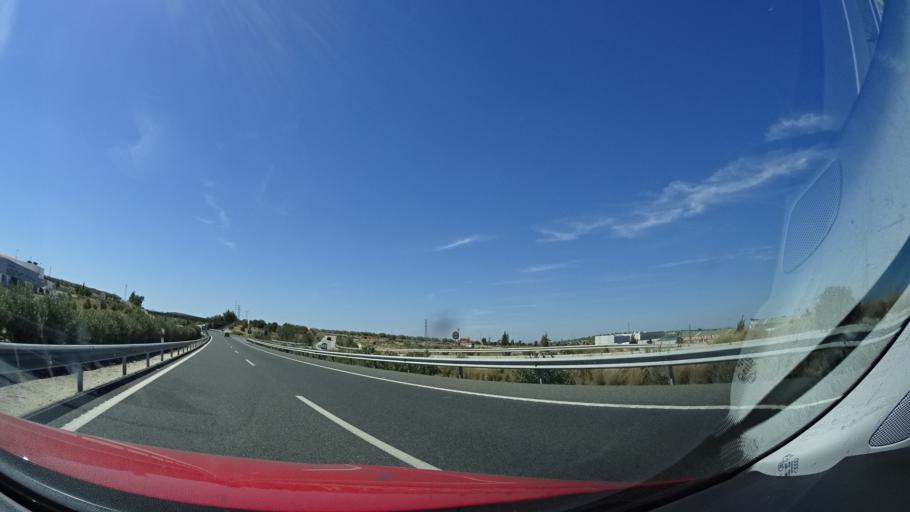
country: ES
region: Andalusia
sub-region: Provincia de Sevilla
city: Estepa
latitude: 37.3026
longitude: -4.8808
